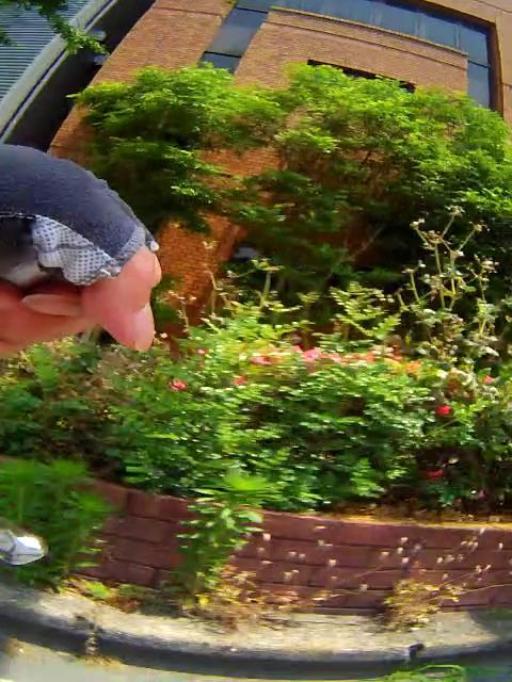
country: JP
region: Osaka
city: Mino
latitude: 34.8195
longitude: 135.4914
